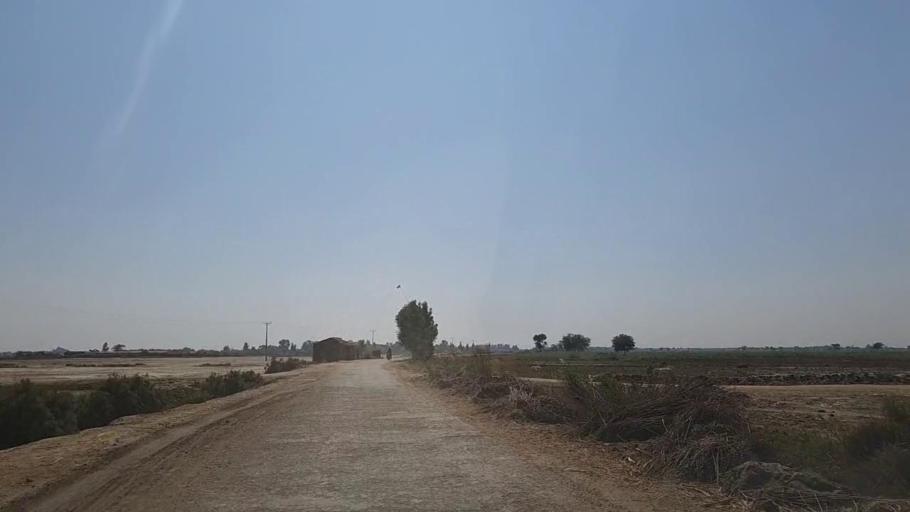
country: PK
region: Sindh
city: Samaro
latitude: 25.3612
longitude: 69.3189
